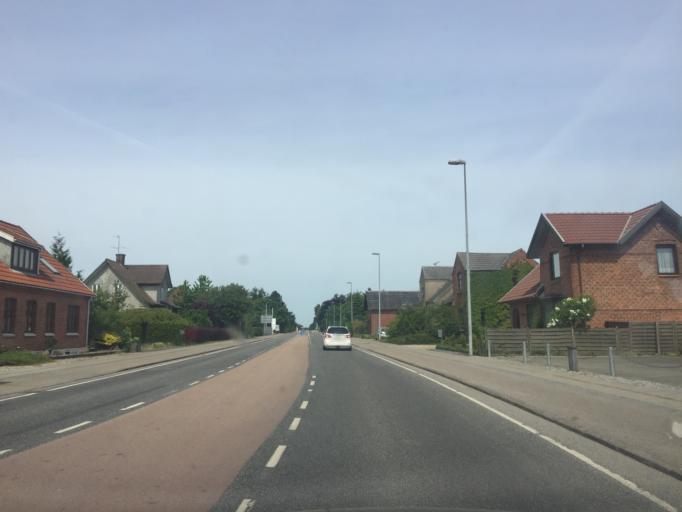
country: DK
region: South Denmark
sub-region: Nyborg Kommune
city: Ullerslev
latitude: 55.2585
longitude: 10.6729
